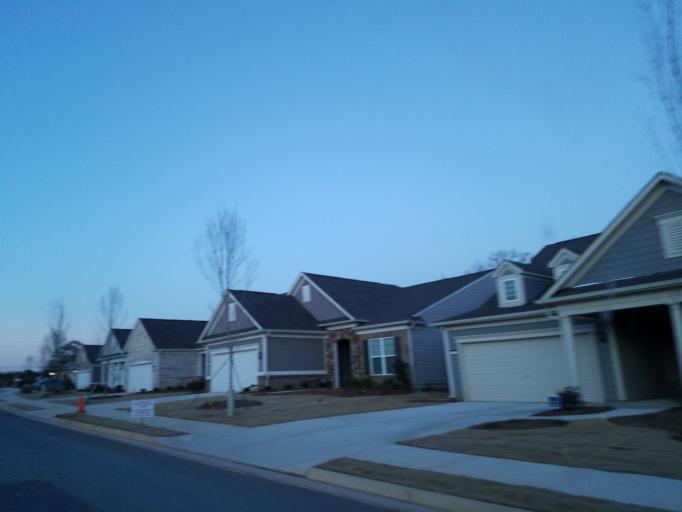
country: US
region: Georgia
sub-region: Cherokee County
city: Holly Springs
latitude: 34.1684
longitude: -84.4204
